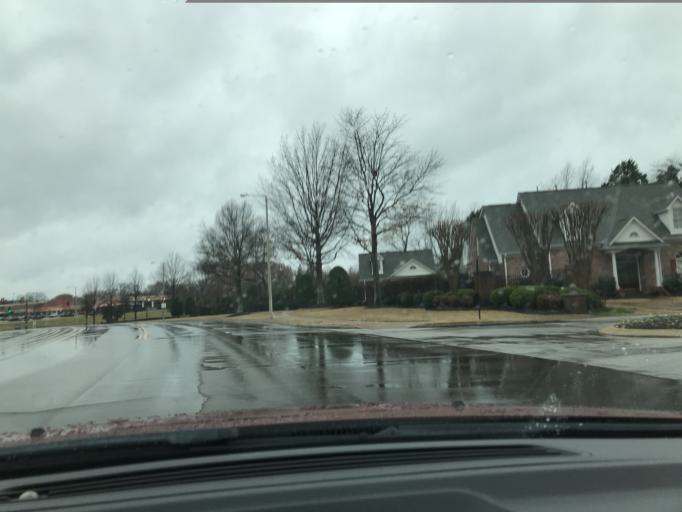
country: US
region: Tennessee
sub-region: Shelby County
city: Collierville
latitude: 35.0534
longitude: -89.6934
